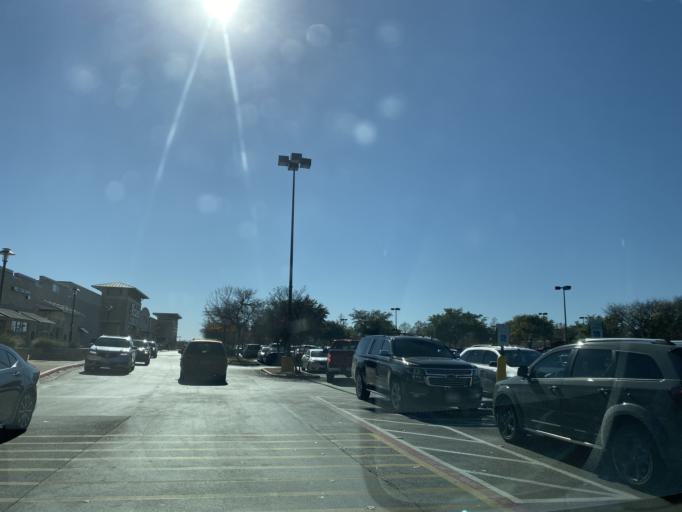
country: US
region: Texas
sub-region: Travis County
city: Windemere
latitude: 30.4791
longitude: -97.6695
